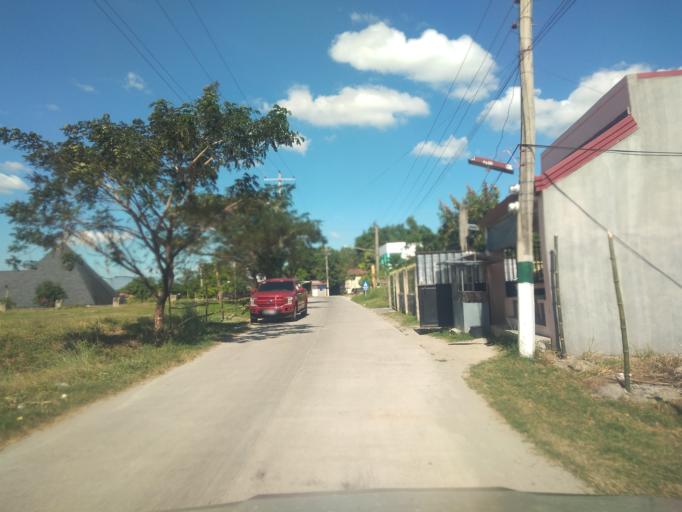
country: PH
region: Central Luzon
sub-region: Province of Pampanga
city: Santa Rita
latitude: 15.0161
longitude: 120.6310
